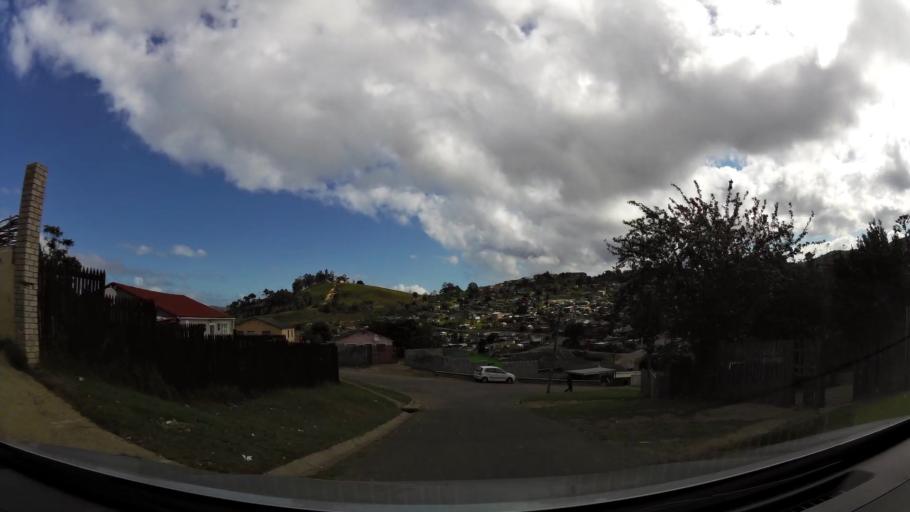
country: ZA
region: Western Cape
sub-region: Eden District Municipality
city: Knysna
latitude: -34.0518
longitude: 23.0956
